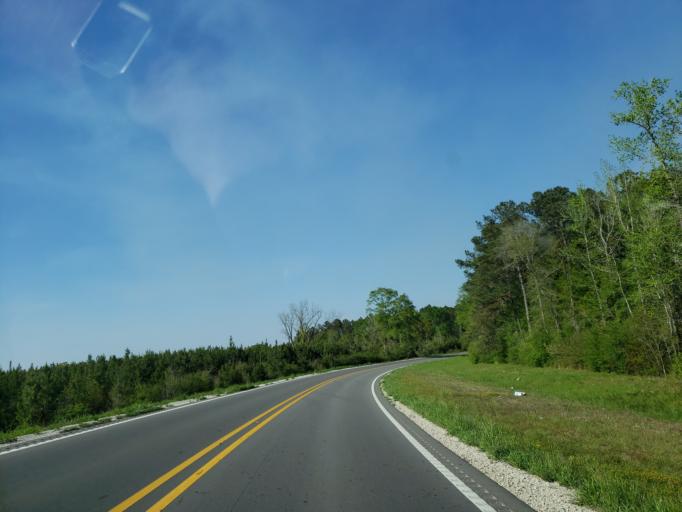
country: US
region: Mississippi
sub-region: Perry County
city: Richton
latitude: 31.3279
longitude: -88.9350
